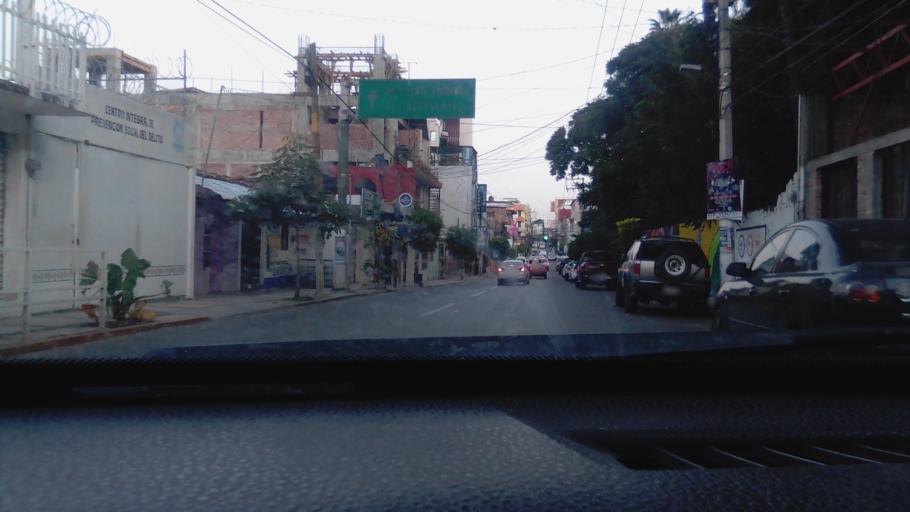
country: MX
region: Guerrero
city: Chilpancingo de los Bravos
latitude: 17.5475
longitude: -99.4979
